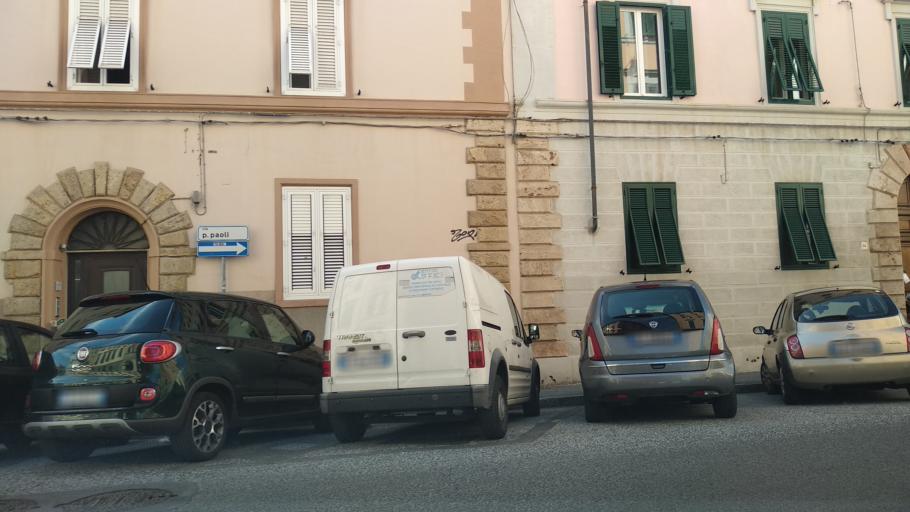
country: IT
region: Tuscany
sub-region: Provincia di Livorno
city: Livorno
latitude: 43.5478
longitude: 10.3188
